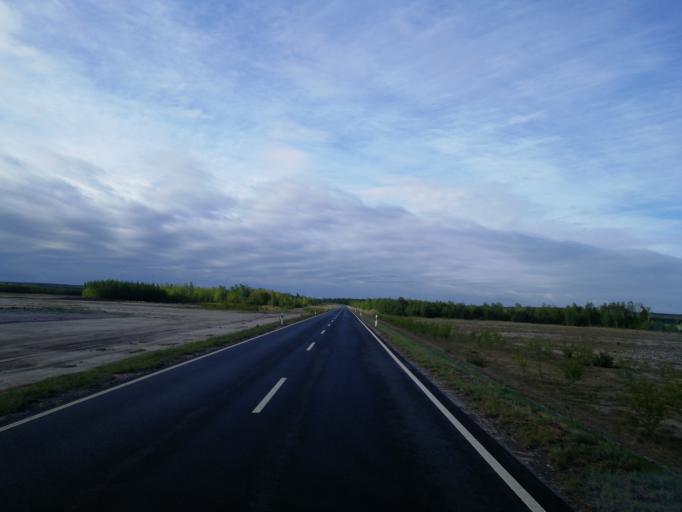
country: DE
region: Brandenburg
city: Lauchhammer
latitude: 51.5523
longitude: 13.7710
